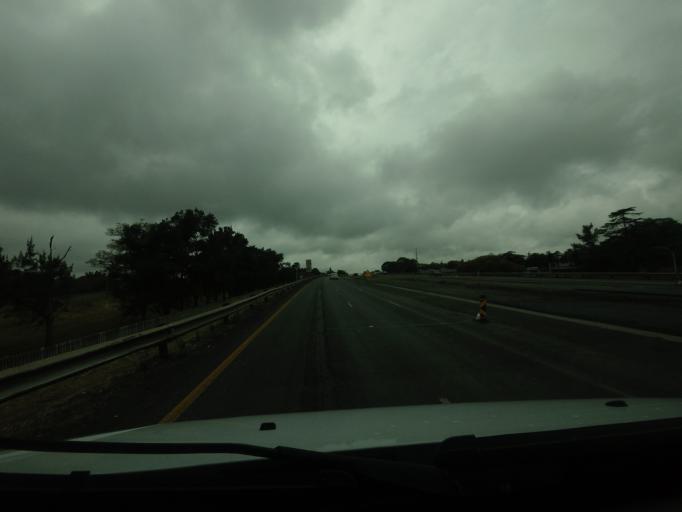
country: ZA
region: Mpumalanga
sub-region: Nkangala District Municipality
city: Witbank
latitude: -25.8852
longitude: 29.2167
